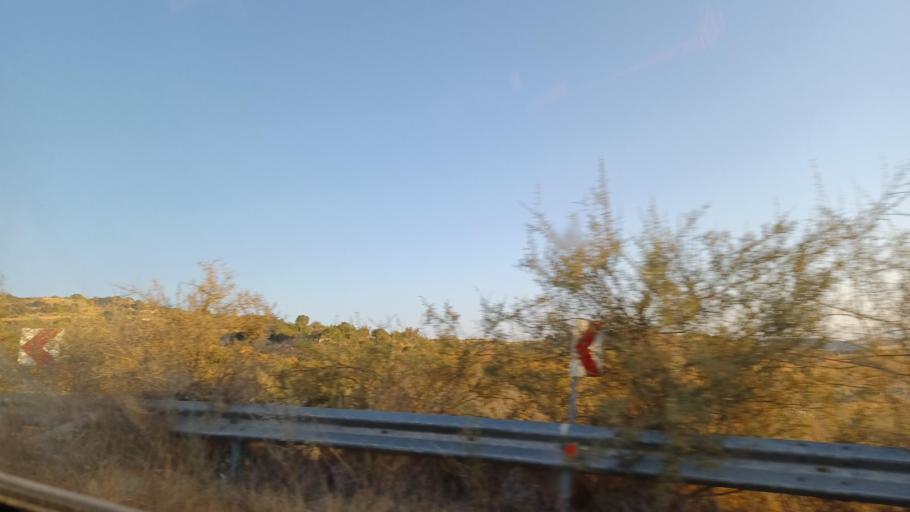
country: CY
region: Pafos
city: Polis
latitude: 35.0033
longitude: 32.4250
